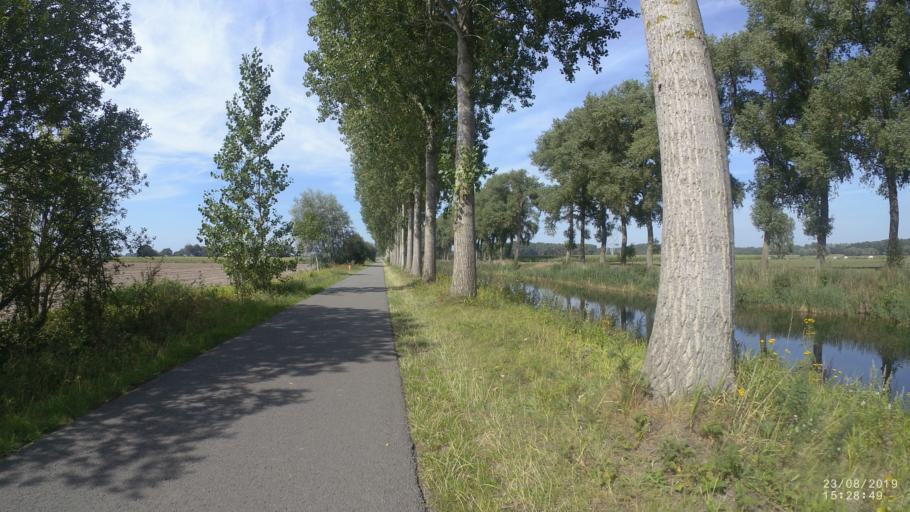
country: BE
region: Flanders
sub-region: Provincie Oost-Vlaanderen
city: Zomergem
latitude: 51.1434
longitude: 3.5562
